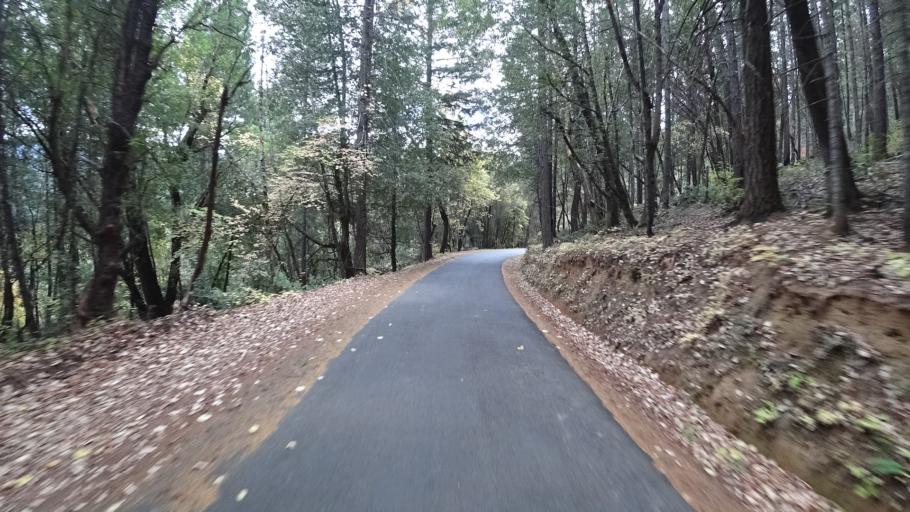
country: US
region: California
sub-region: Siskiyou County
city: Happy Camp
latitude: 41.8024
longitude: -123.3544
